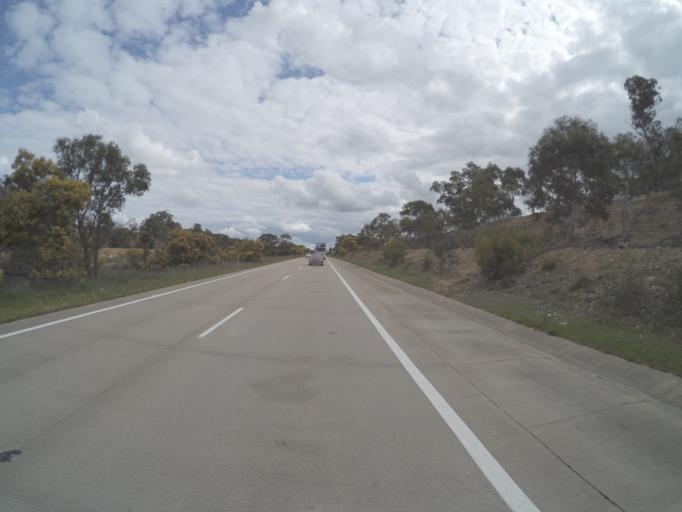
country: AU
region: New South Wales
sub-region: Goulburn Mulwaree
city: Goulburn
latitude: -34.8050
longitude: 149.4917
